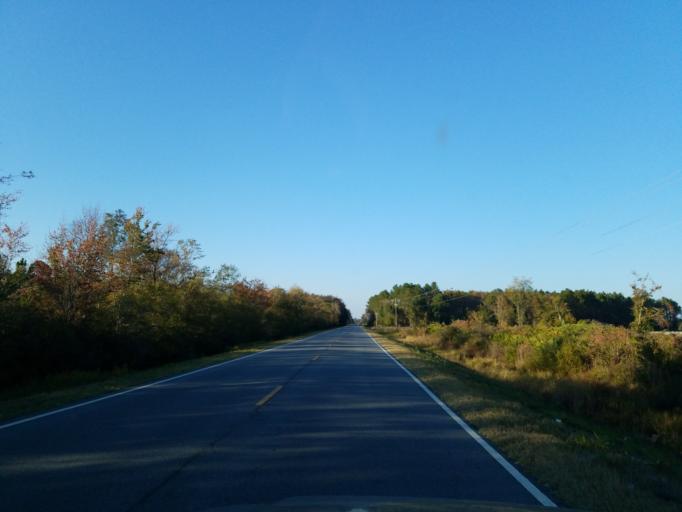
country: US
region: Georgia
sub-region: Lanier County
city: Lakeland
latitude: 31.1113
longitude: -83.0816
